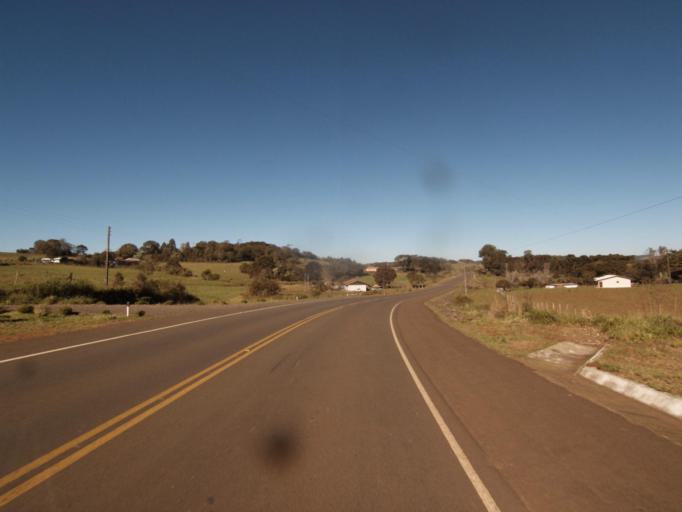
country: AR
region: Misiones
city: Bernardo de Irigoyen
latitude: -26.6715
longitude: -53.5708
